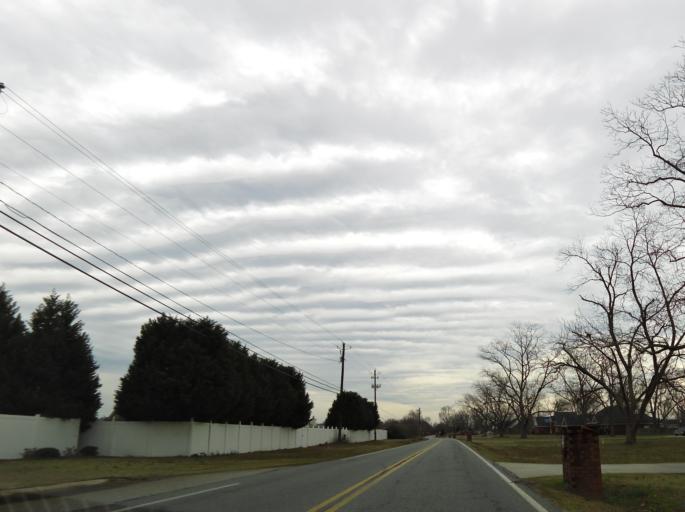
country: US
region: Georgia
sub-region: Houston County
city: Centerville
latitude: 32.7169
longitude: -83.6975
